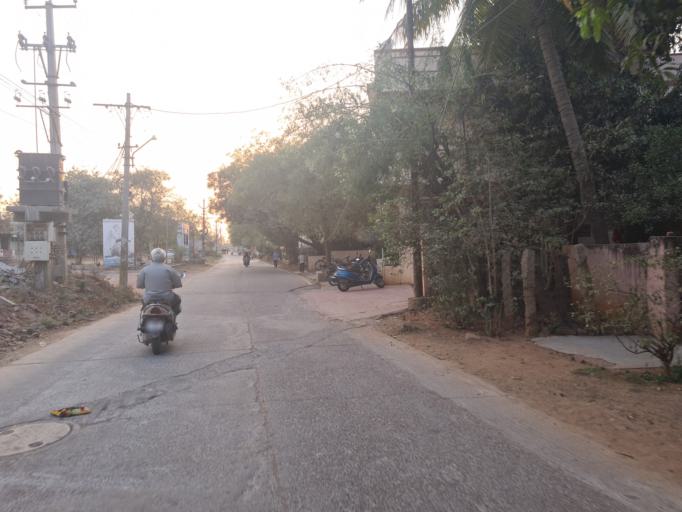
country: IN
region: Telangana
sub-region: Medak
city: Serilingampalle
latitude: 17.4802
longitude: 78.3022
